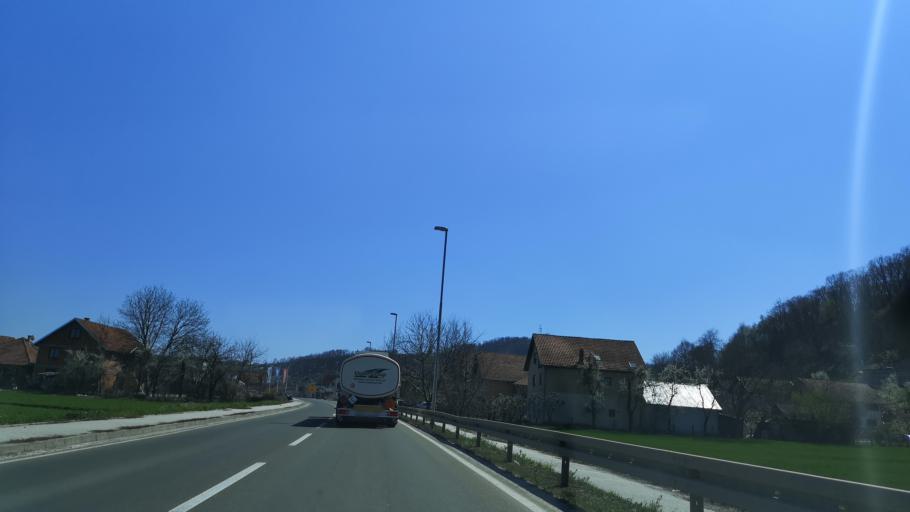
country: RS
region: Central Serbia
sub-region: Moravicki Okrug
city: Cacak
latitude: 43.8868
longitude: 20.3160
